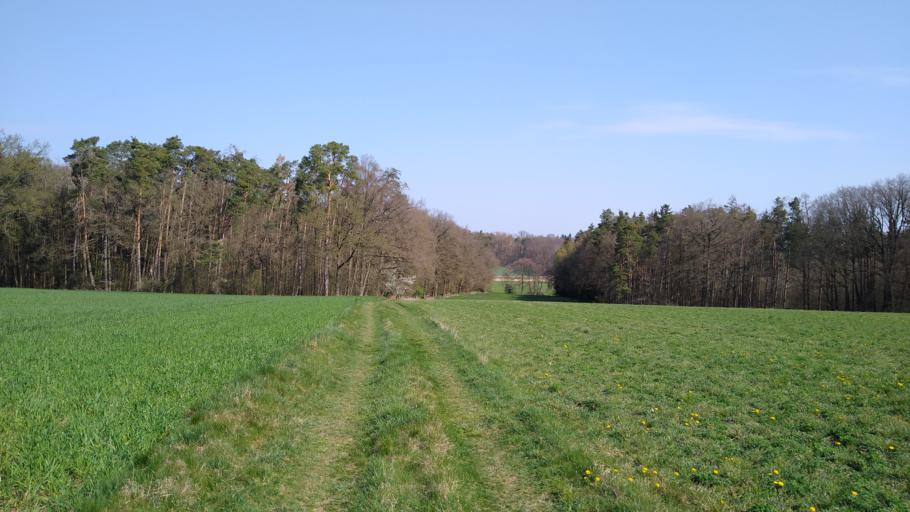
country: DE
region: Bavaria
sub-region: Regierungsbezirk Mittelfranken
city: Obermichelbach
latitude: 49.5037
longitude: 10.9216
